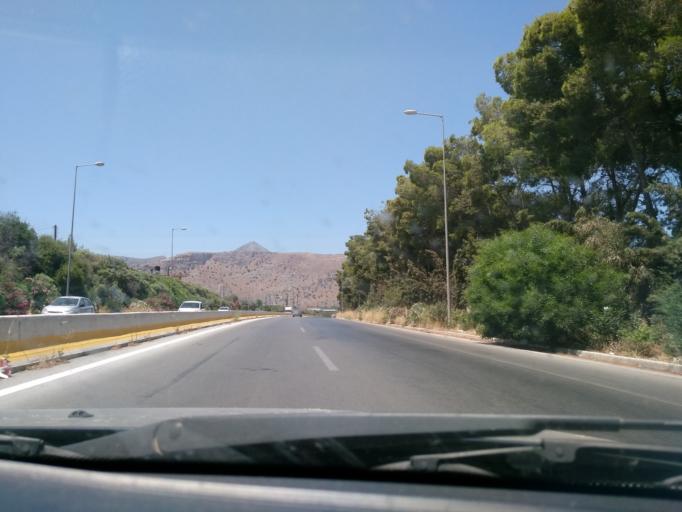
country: GR
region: Crete
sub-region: Nomos Irakleiou
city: Gazi
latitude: 35.3180
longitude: 25.0717
